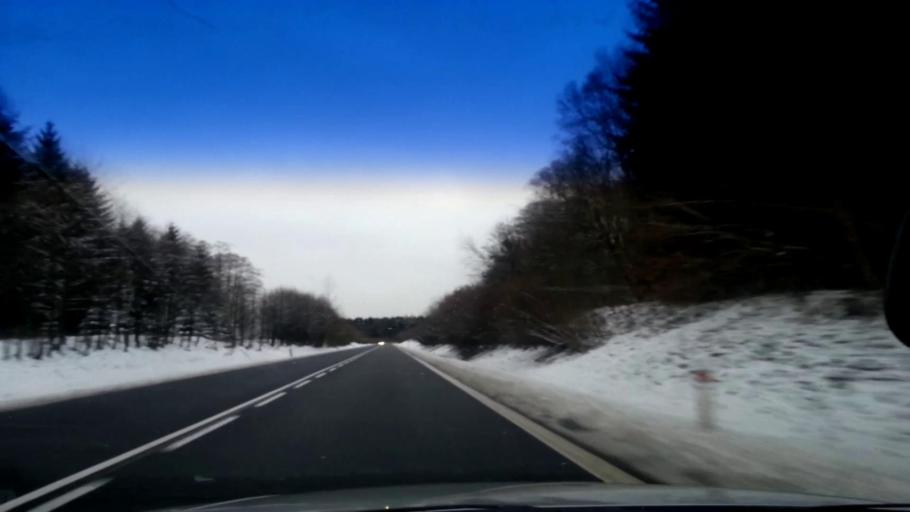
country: CZ
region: Karlovarsky
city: As
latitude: 50.2069
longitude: 12.1899
